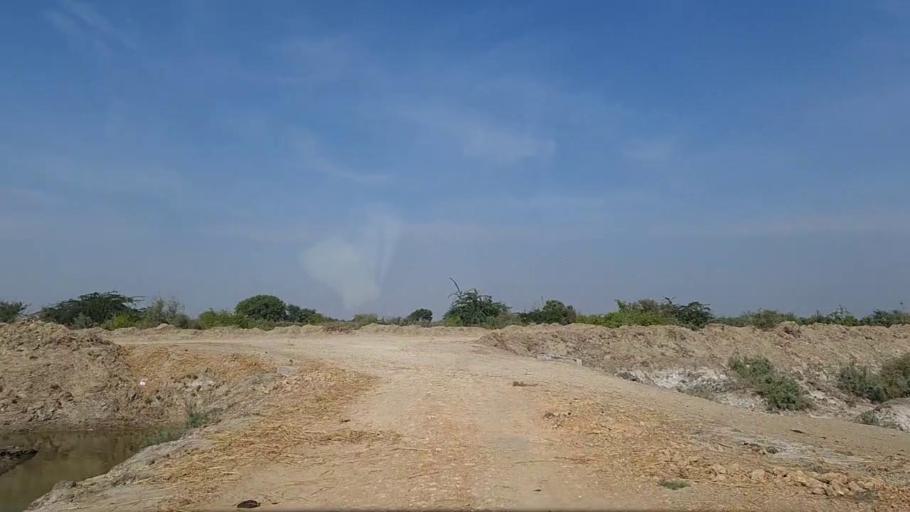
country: PK
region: Sindh
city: Daro Mehar
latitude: 24.7090
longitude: 68.1498
